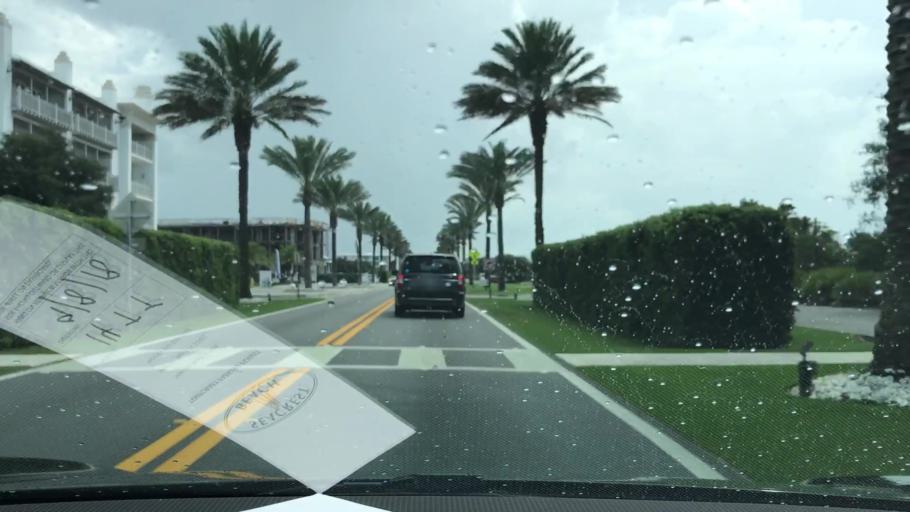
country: US
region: Florida
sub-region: Bay County
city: Laguna Beach
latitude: 30.2850
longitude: -86.0297
